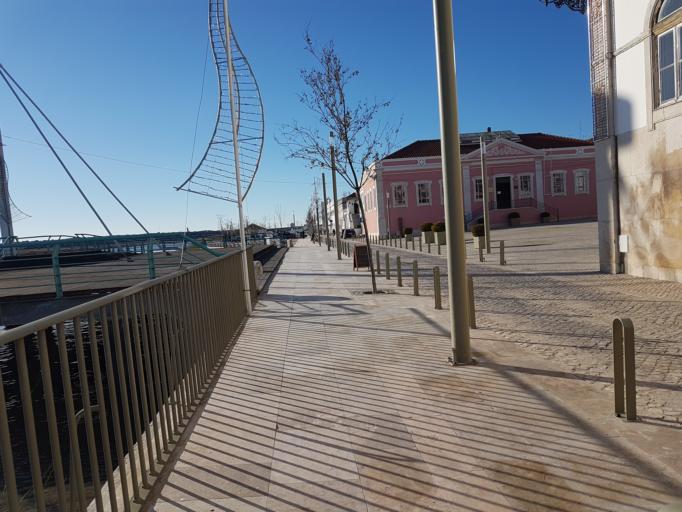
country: PT
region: Setubal
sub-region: Alcacer do Sal
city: Alcacer do Sal
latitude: 38.3707
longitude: -8.5127
